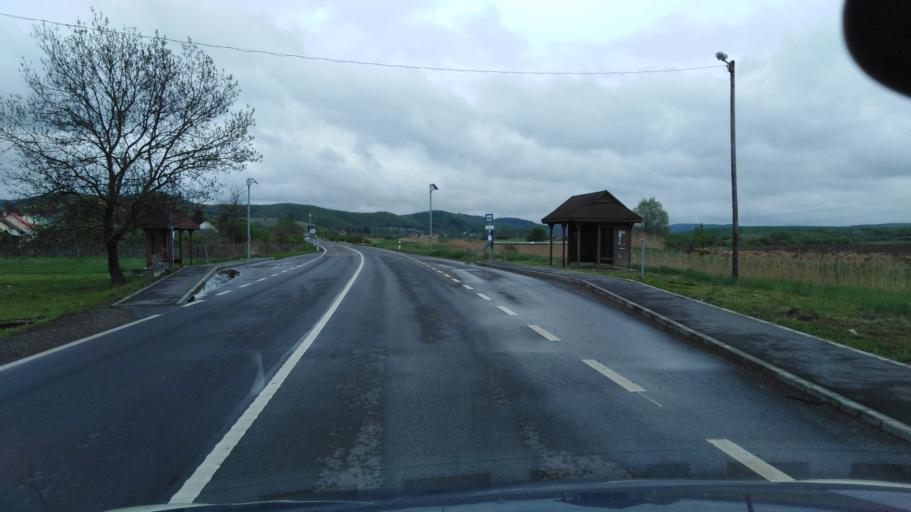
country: HU
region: Nograd
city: Karancskeszi
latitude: 48.1145
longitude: 19.6562
